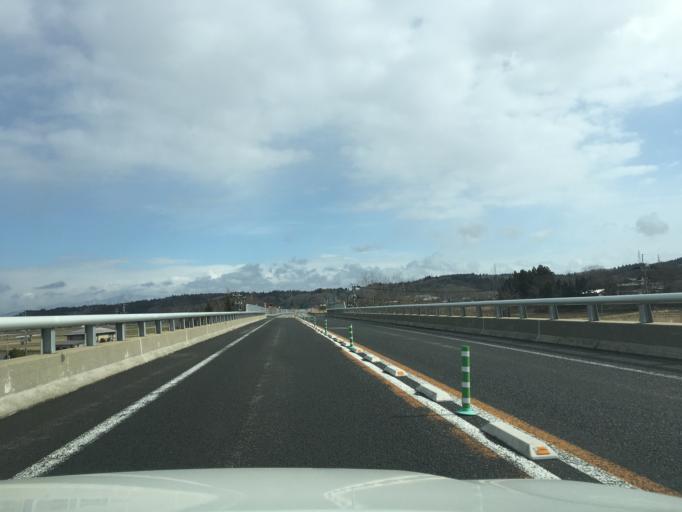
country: JP
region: Akita
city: Akita
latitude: 39.6221
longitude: 140.1523
